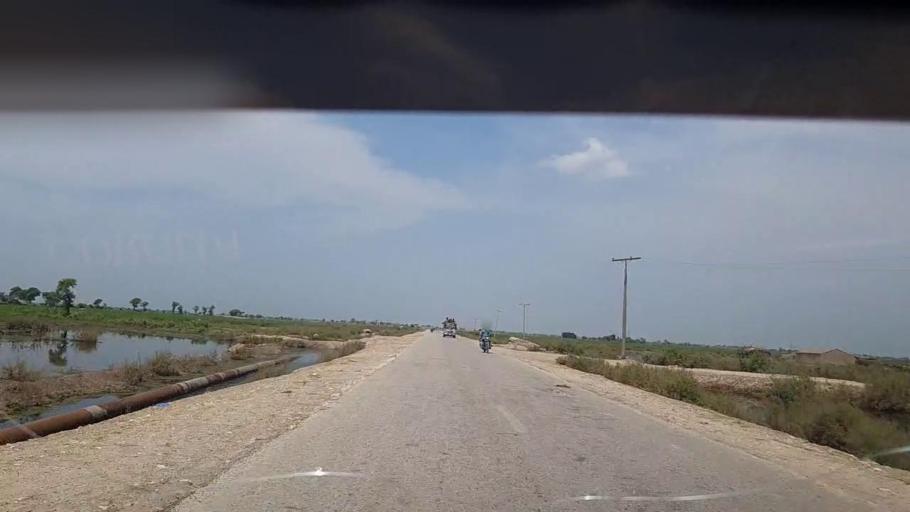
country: PK
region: Sindh
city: Thul
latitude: 28.1885
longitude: 68.7966
